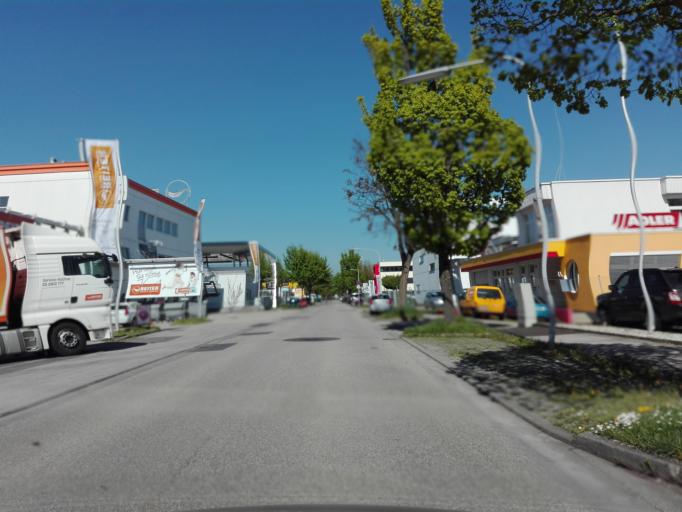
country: AT
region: Upper Austria
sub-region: Politischer Bezirk Linz-Land
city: Leonding
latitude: 48.2572
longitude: 14.2548
